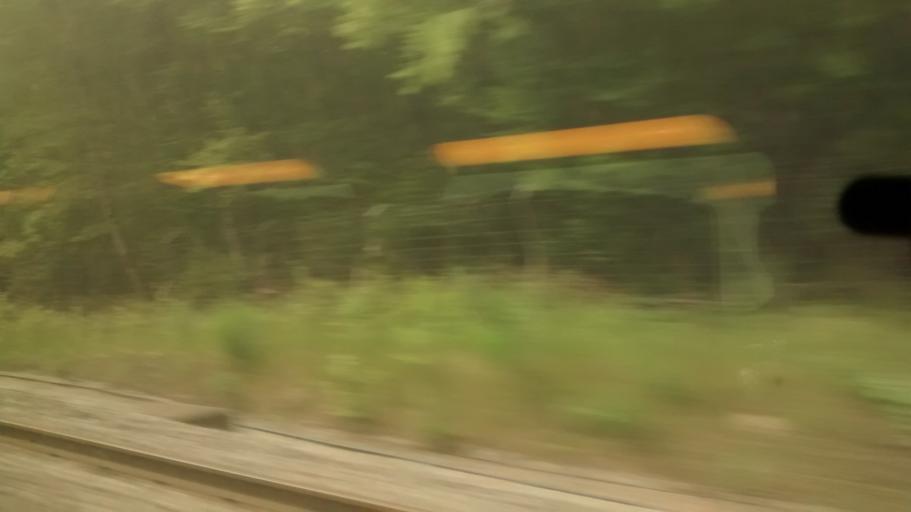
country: FR
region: Bourgogne
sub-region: Departement de Saone-et-Loire
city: Saint-Sernin-du-Bois
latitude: 46.8965
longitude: 4.4889
